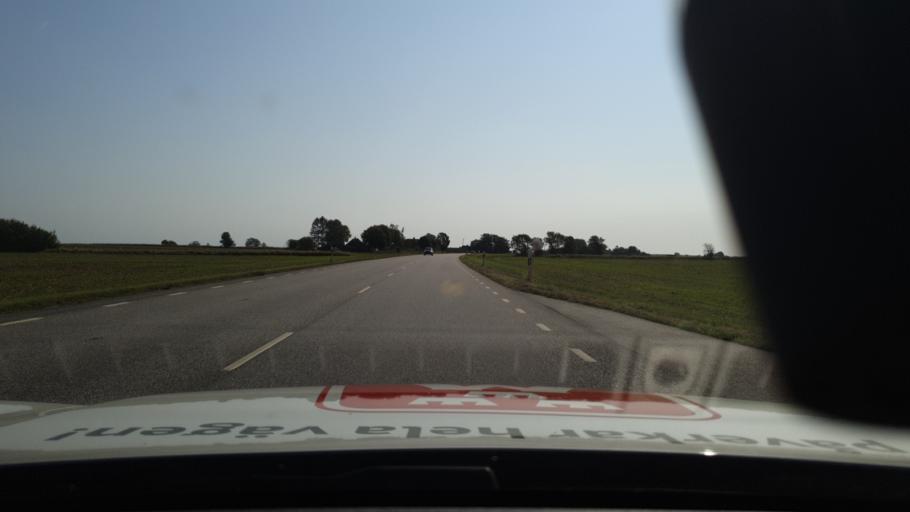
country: SE
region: Skane
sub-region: Kristianstads Kommun
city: Norra Asum
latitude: 55.9774
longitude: 14.1738
